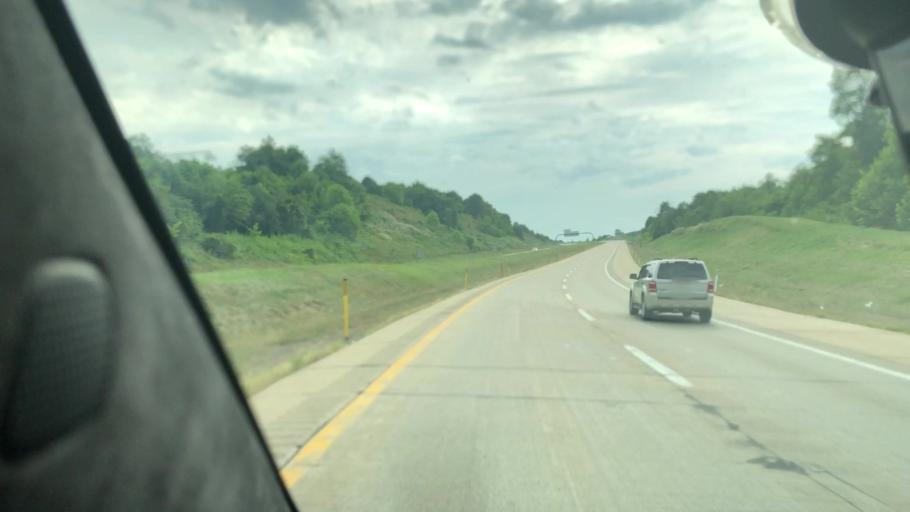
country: US
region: Pennsylvania
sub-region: Allegheny County
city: Jefferson Hills
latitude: 40.2785
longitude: -79.9383
